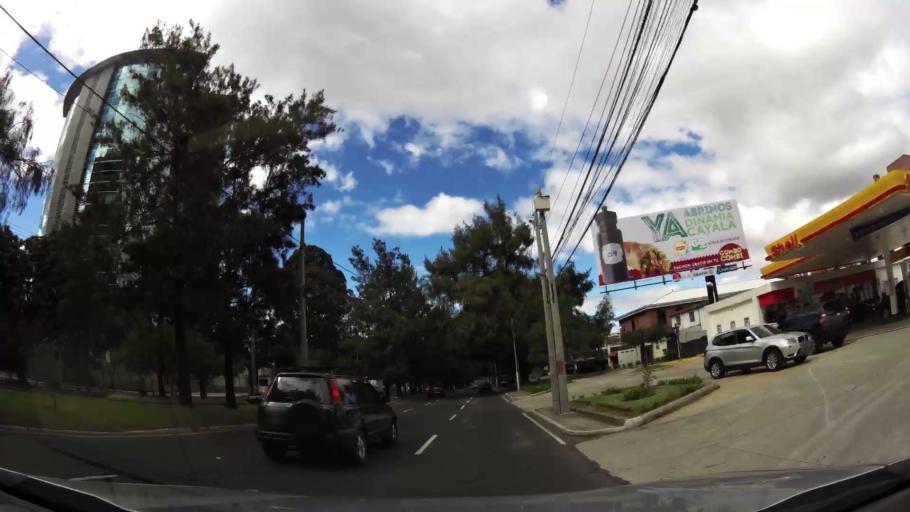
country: GT
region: Guatemala
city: Santa Catarina Pinula
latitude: 14.5836
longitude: -90.4863
